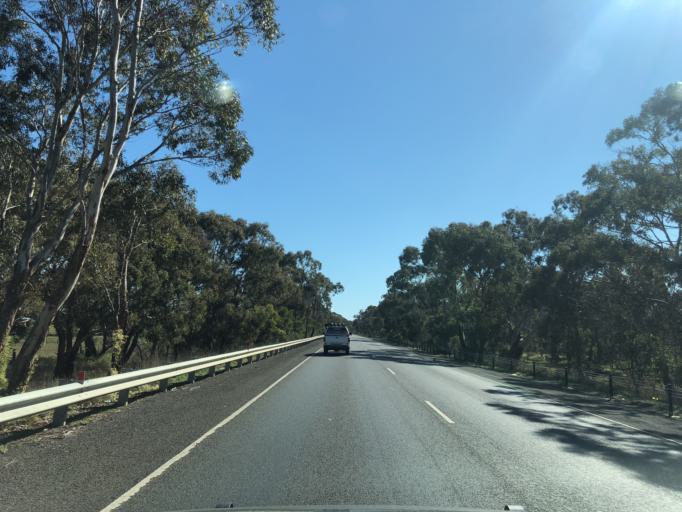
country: AU
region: Victoria
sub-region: Melton
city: Kurunjang
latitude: -37.6175
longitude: 144.6207
